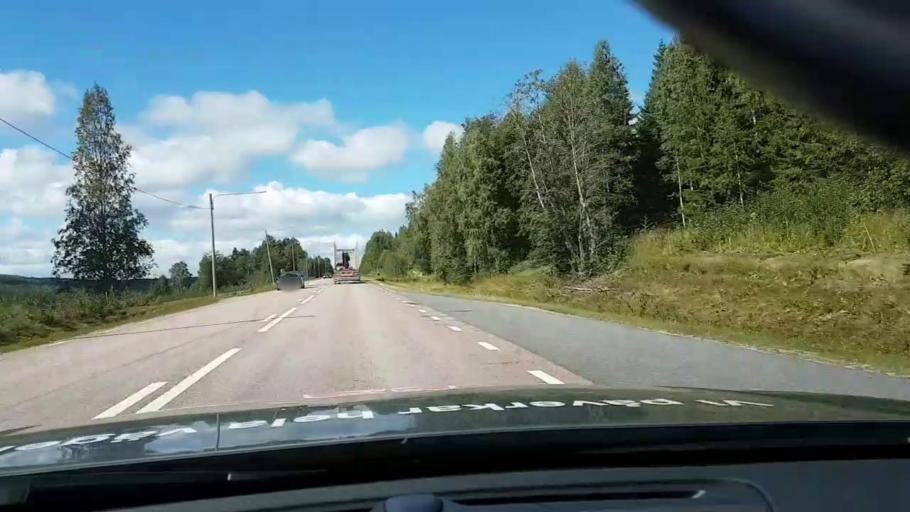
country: SE
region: Vaesternorrland
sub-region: OErnskoeldsviks Kommun
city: Bjasta
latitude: 63.3824
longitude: 18.4045
